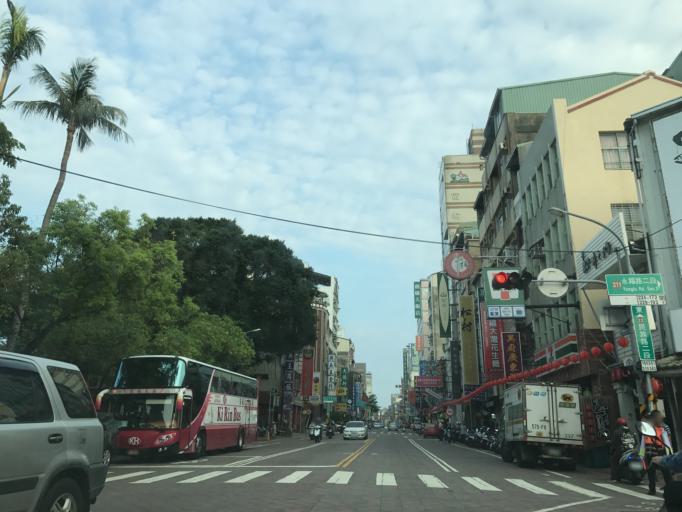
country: TW
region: Taiwan
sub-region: Tainan
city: Tainan
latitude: 22.9969
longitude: 120.2024
